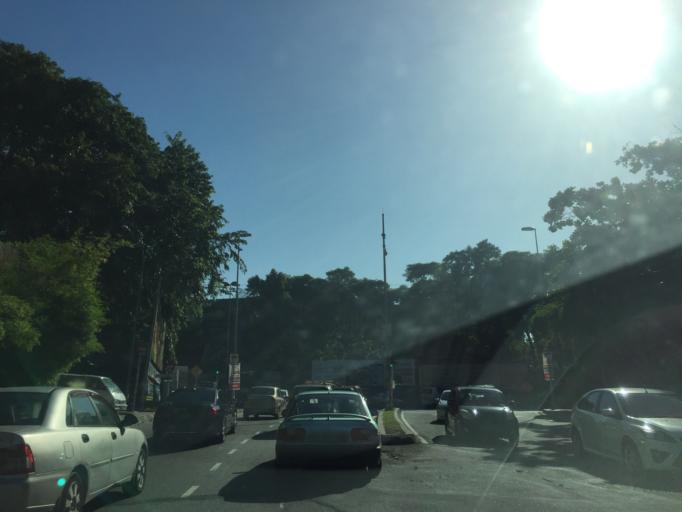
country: MY
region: Selangor
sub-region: Petaling
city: Petaling Jaya
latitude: 3.1190
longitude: 101.6288
